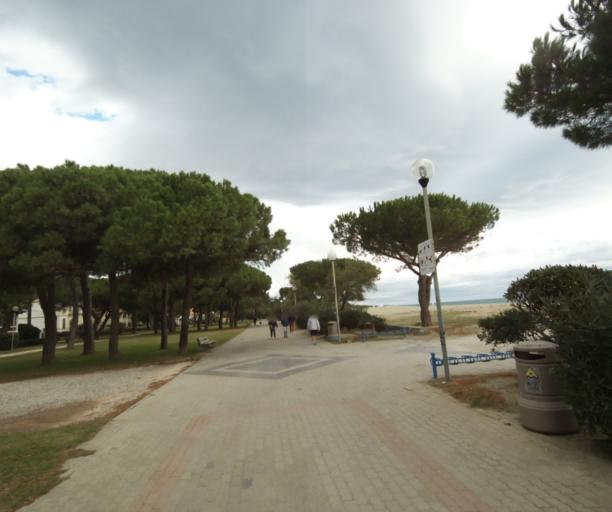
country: FR
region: Languedoc-Roussillon
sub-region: Departement des Pyrenees-Orientales
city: Argelers
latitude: 42.5469
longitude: 3.0496
